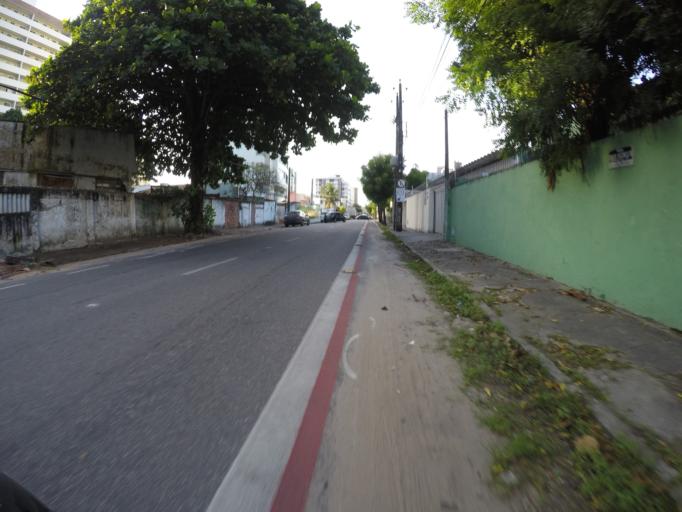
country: BR
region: Ceara
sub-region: Fortaleza
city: Fortaleza
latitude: -3.7459
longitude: -38.5149
